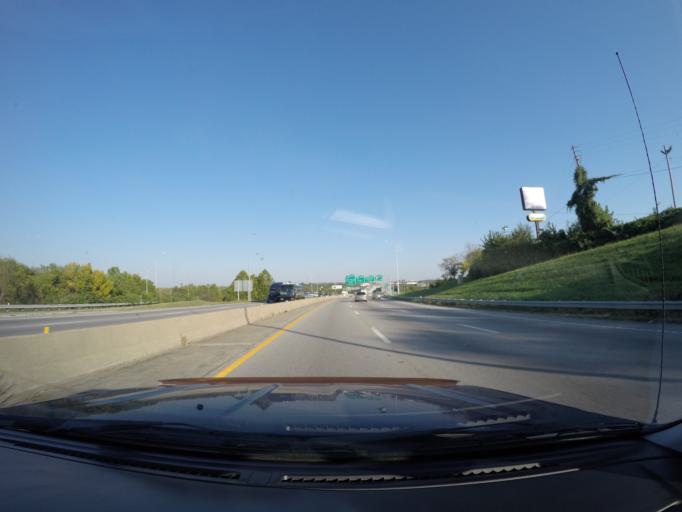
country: US
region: Missouri
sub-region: Jackson County
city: Kansas City
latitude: 39.0697
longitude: -94.5135
